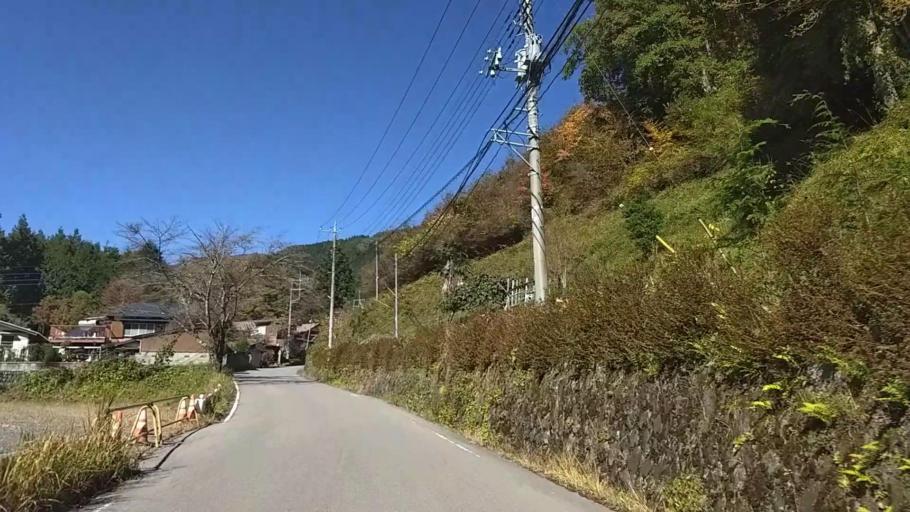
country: JP
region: Yamanashi
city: Uenohara
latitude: 35.7008
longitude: 139.0233
